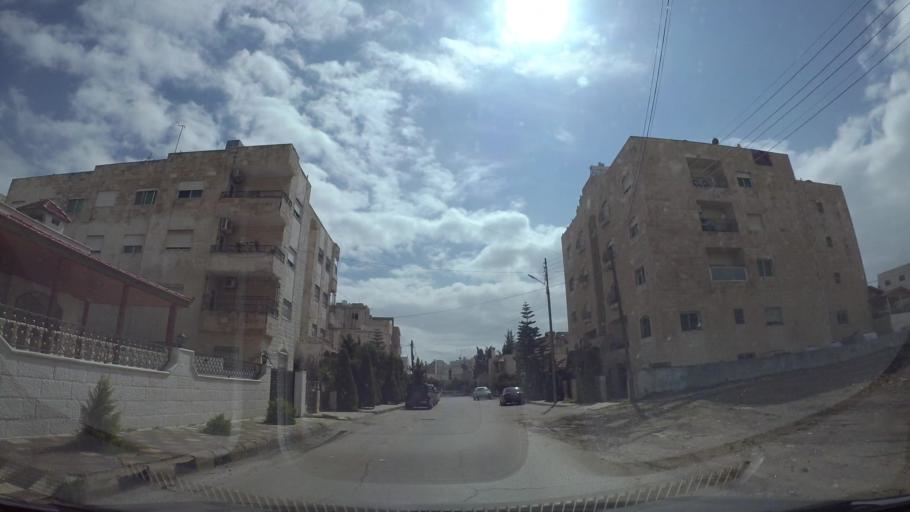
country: JO
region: Amman
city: Wadi as Sir
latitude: 31.9588
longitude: 35.8404
